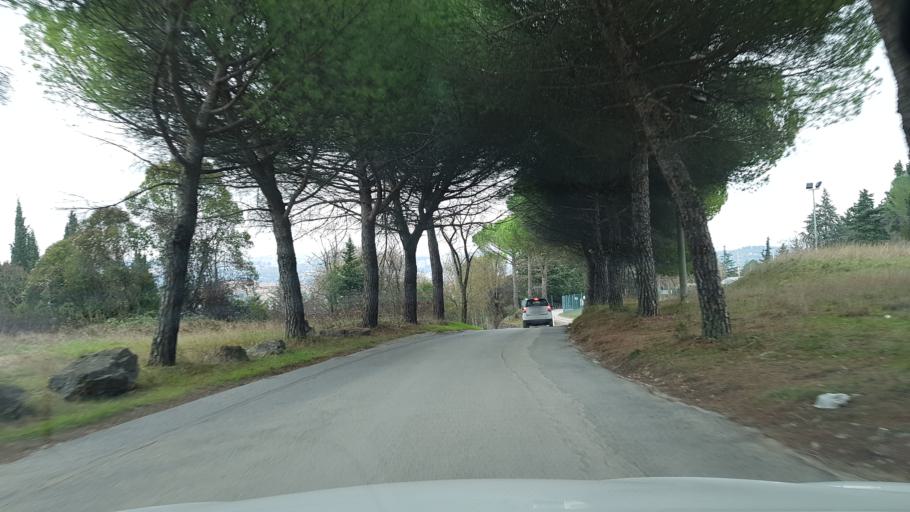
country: IT
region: Umbria
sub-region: Provincia di Perugia
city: Lacugnano
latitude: 43.1035
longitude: 12.3335
